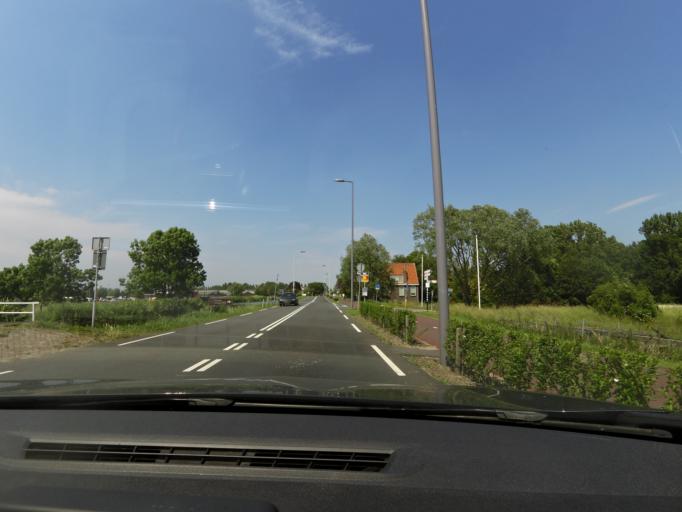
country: NL
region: South Holland
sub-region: Gemeente Lansingerland
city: Bergschenhoek
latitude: 51.9707
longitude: 4.4957
